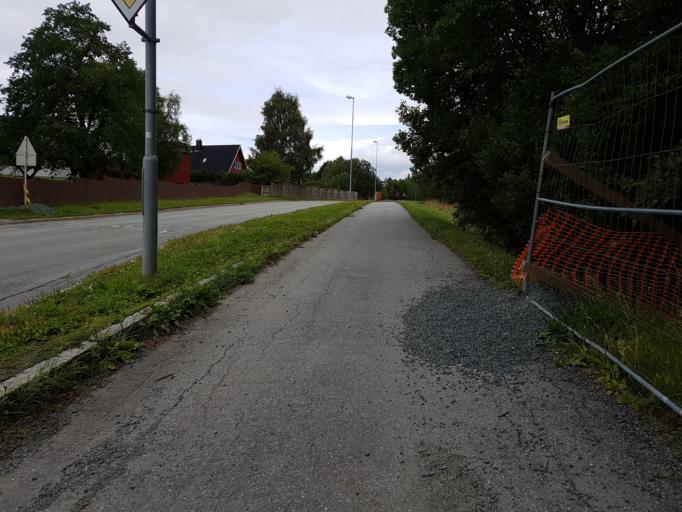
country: NO
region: Sor-Trondelag
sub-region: Trondheim
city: Trondheim
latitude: 63.3944
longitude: 10.4395
